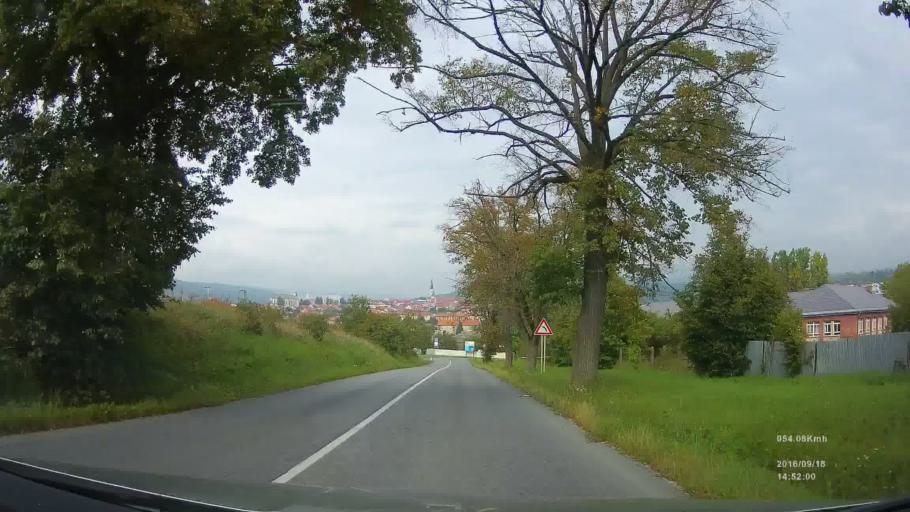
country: SK
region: Presovsky
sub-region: Okres Presov
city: Levoca
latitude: 49.0140
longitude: 20.5867
